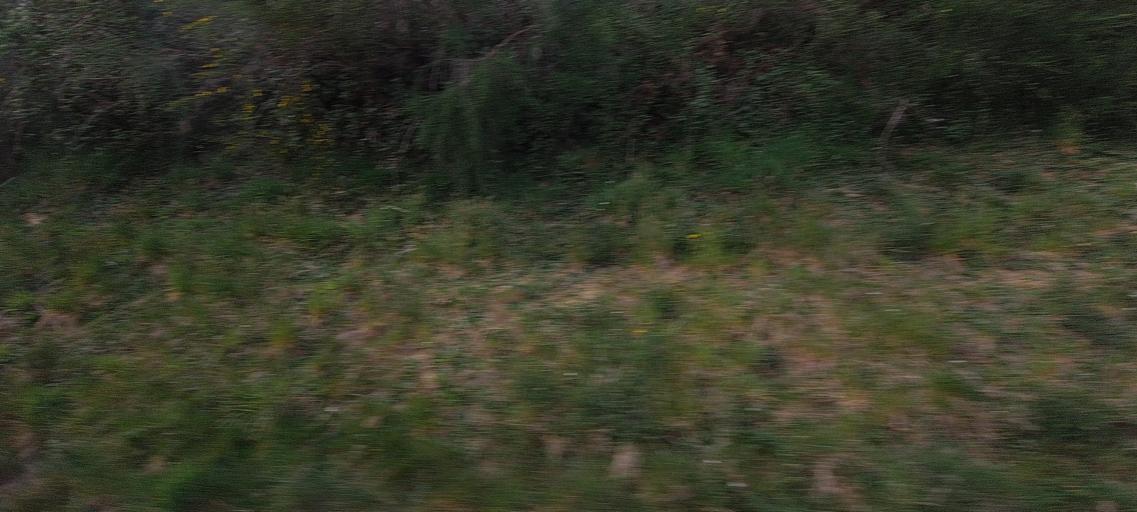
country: US
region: Oregon
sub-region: Clatsop County
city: Astoria
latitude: 46.1809
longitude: -123.8173
